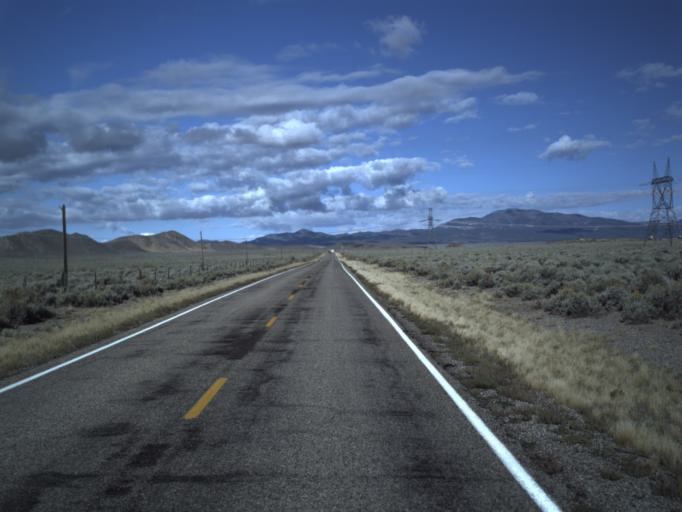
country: US
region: Utah
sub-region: Beaver County
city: Milford
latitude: 38.4083
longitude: -113.0567
